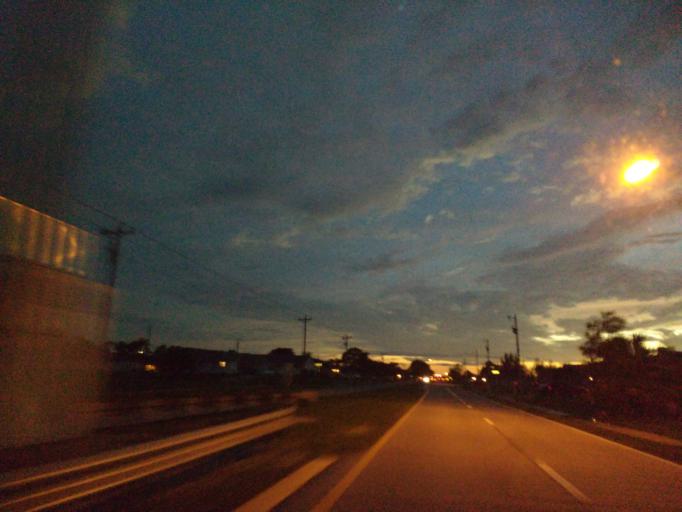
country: US
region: Florida
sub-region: Lee County
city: Cape Coral
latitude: 26.6227
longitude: -82.0006
